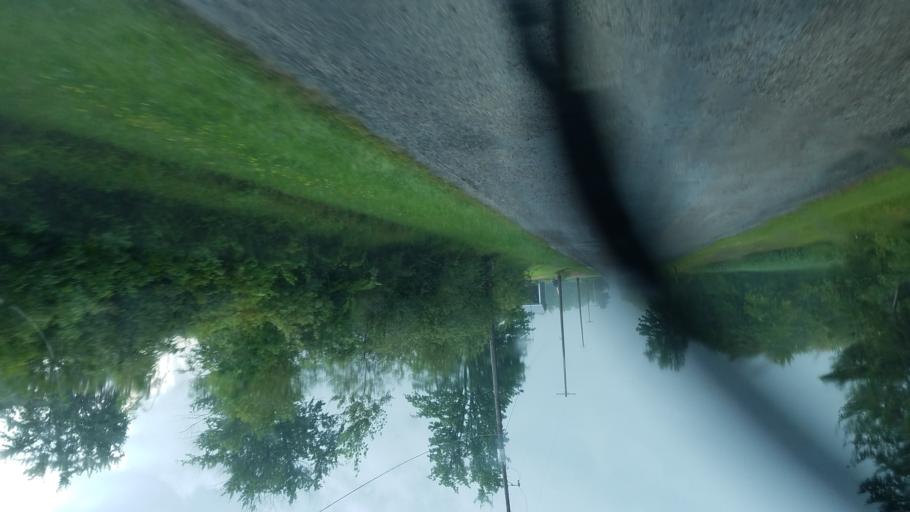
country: US
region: Ohio
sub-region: Geauga County
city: Middlefield
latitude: 41.5238
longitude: -80.9825
